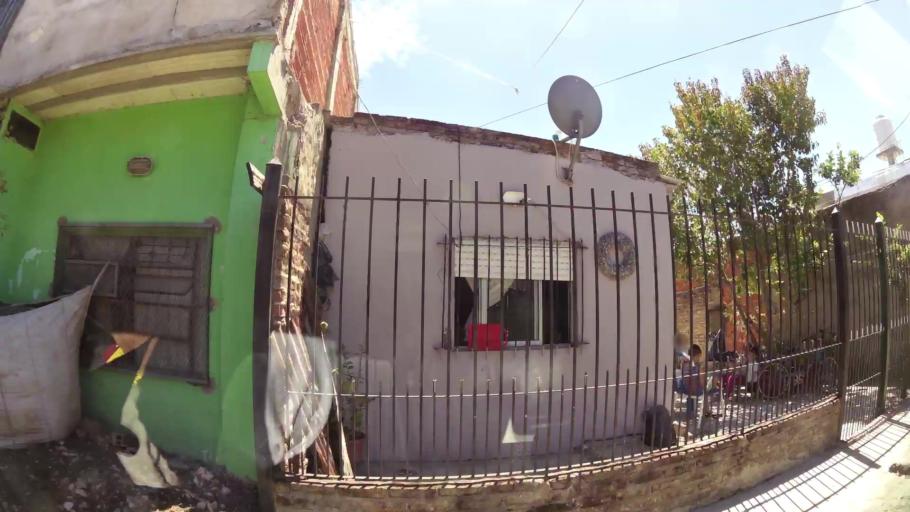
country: AR
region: Buenos Aires
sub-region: Partido de Quilmes
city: Quilmes
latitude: -34.7215
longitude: -58.3241
